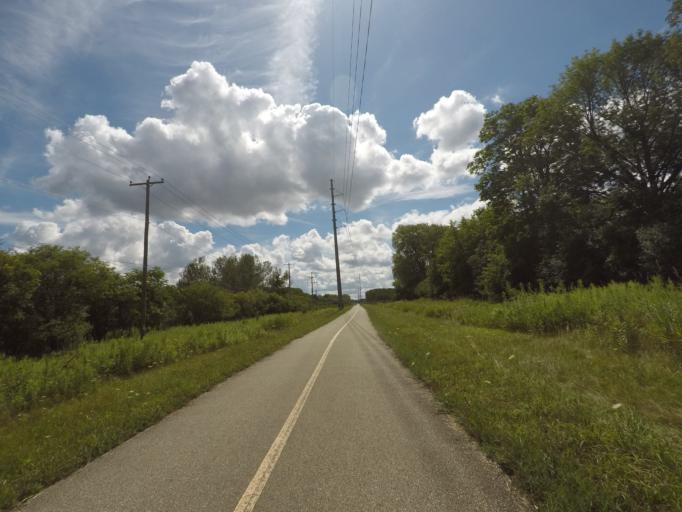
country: US
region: Wisconsin
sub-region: Waukesha County
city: Pewaukee
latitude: 43.0601
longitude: -88.2983
